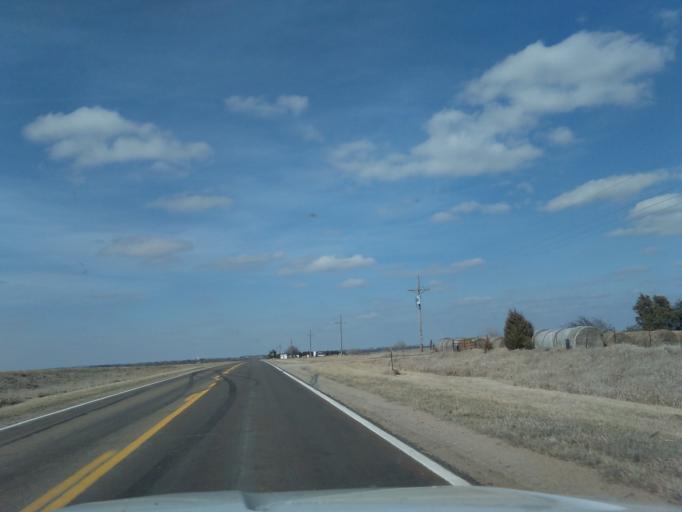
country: US
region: Nebraska
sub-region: Jefferson County
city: Fairbury
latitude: 40.0814
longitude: -96.9351
